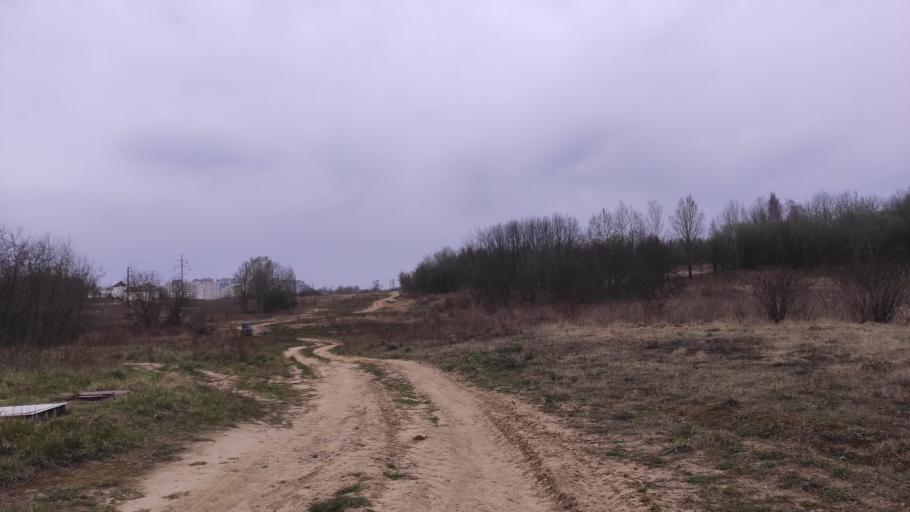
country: BY
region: Minsk
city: Novoye Medvezhino
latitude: 53.8865
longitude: 27.4646
